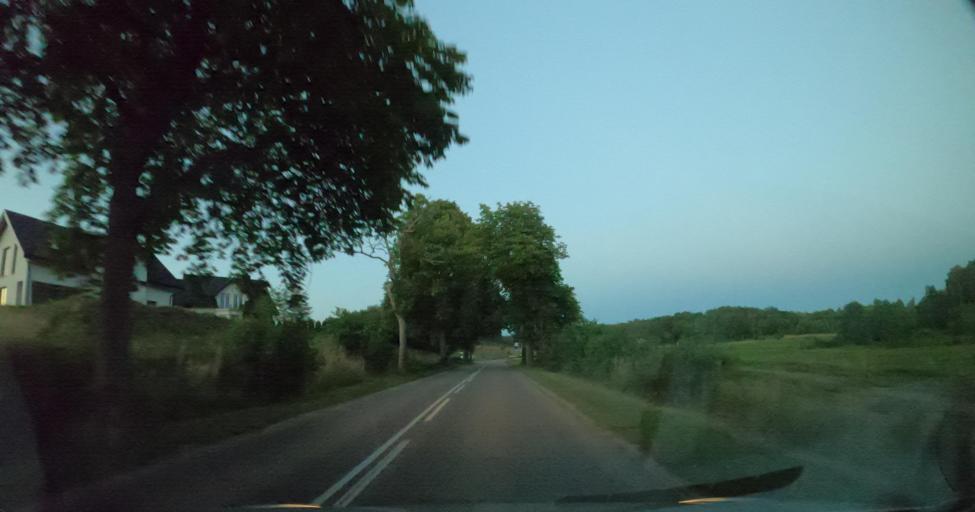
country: PL
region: Pomeranian Voivodeship
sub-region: Powiat wejherowski
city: Koleczkowo
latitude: 54.4686
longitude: 18.3088
